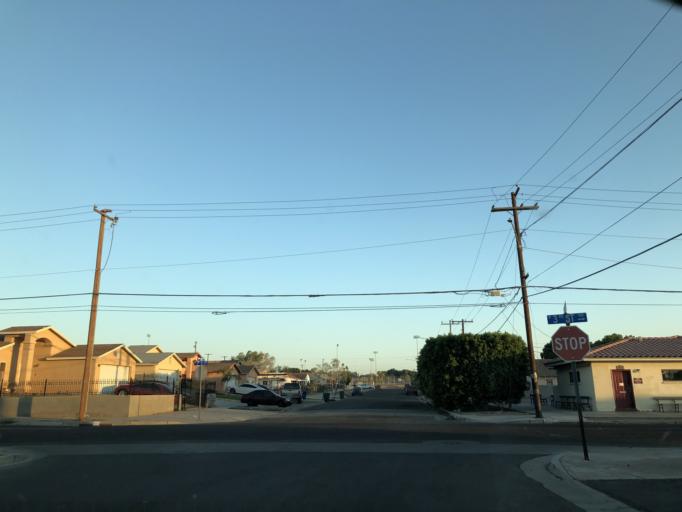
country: US
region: Arizona
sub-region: Yuma County
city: Yuma
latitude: 32.7218
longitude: -114.6308
